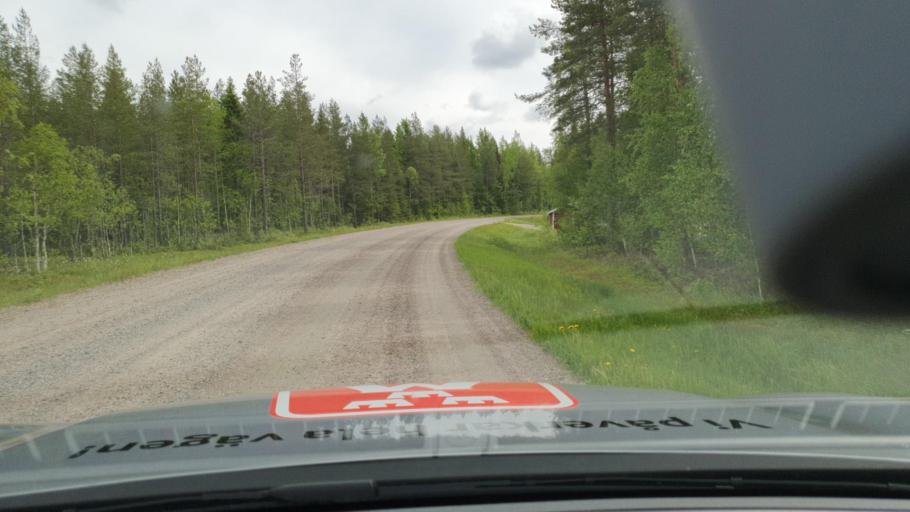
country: FI
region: Lapland
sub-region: Torniolaakso
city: Ylitornio
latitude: 65.9630
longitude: 23.7228
